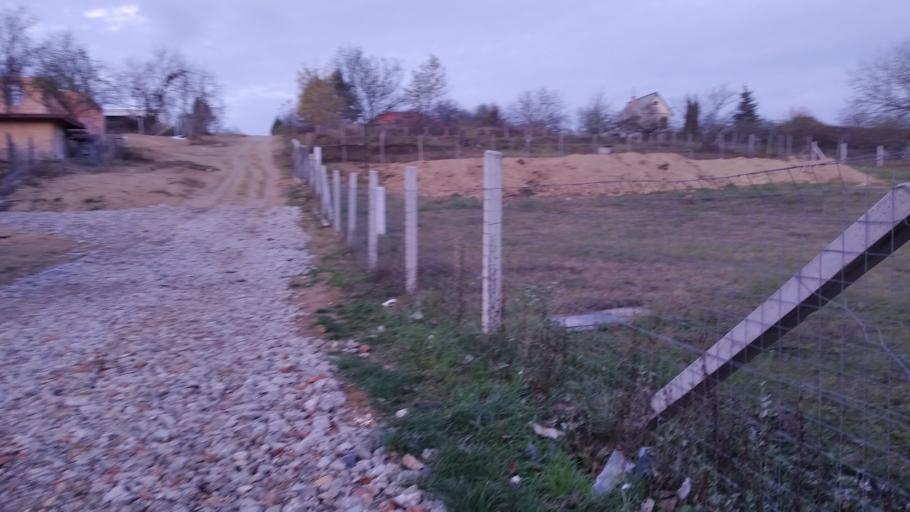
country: HU
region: Pest
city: Budakalasz
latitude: 47.6244
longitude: 19.0344
